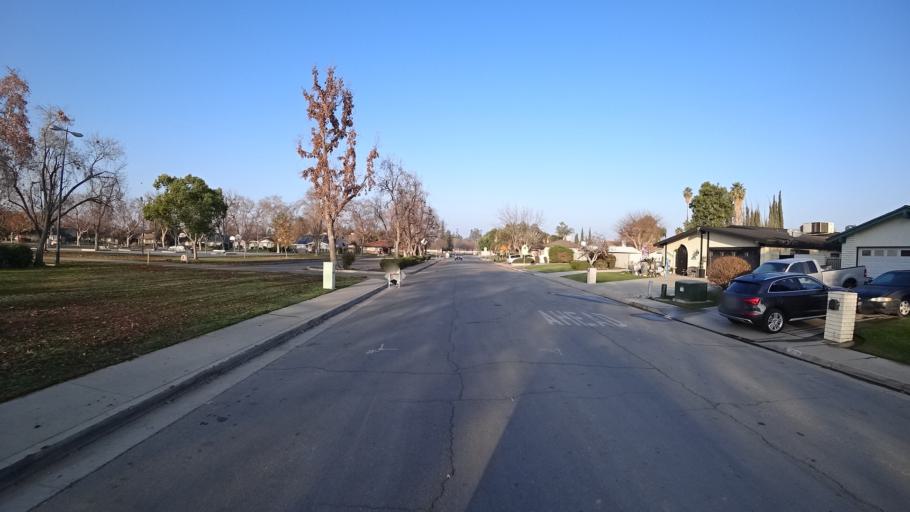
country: US
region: California
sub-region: Kern County
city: Bakersfield
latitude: 35.3613
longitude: -119.0531
